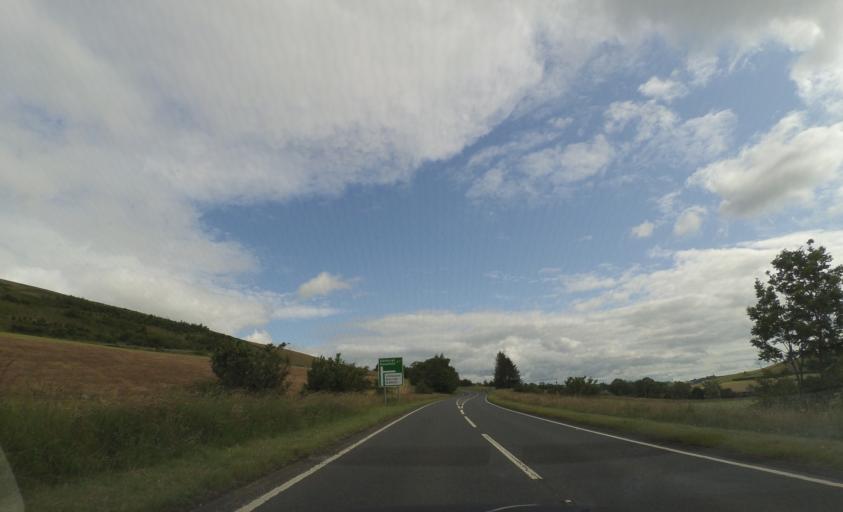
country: GB
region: Scotland
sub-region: The Scottish Borders
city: Selkirk
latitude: 55.4955
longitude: -2.8349
